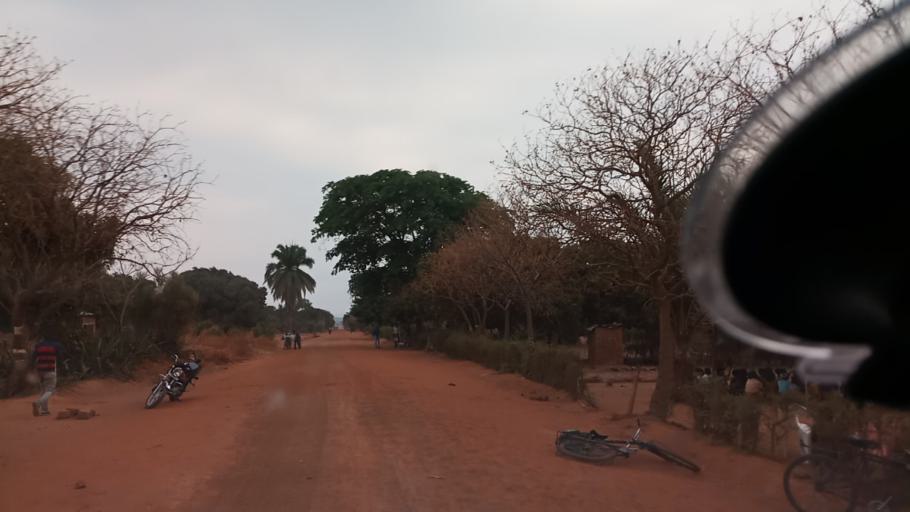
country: ZM
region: Luapula
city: Nchelenge
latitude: -9.2770
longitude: 28.3269
